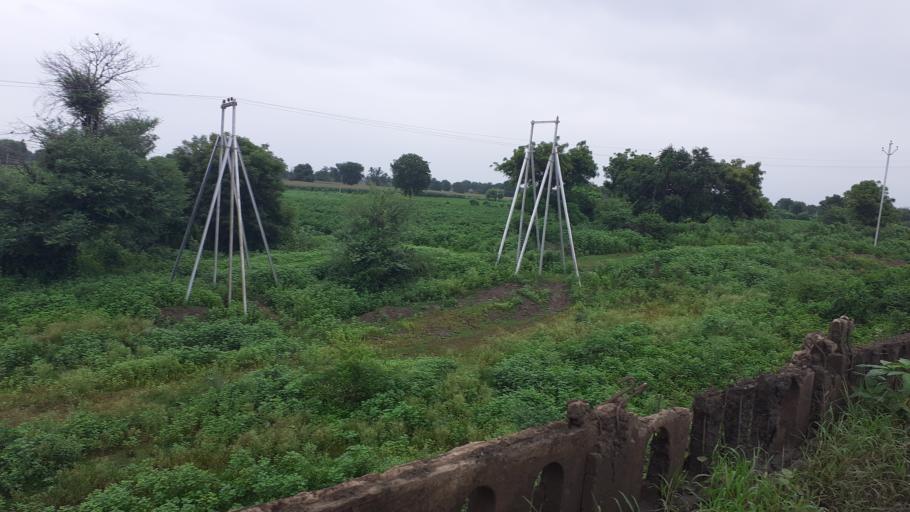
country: IN
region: Maharashtra
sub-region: Buldana
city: Nandura
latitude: 20.8004
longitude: 76.4894
